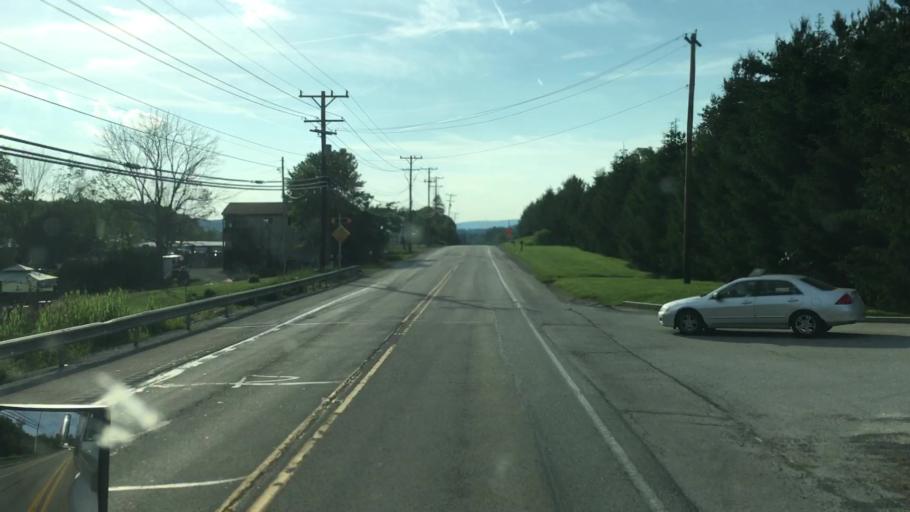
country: US
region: Pennsylvania
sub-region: Fayette County
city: Hopwood
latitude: 39.7967
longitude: -79.5435
